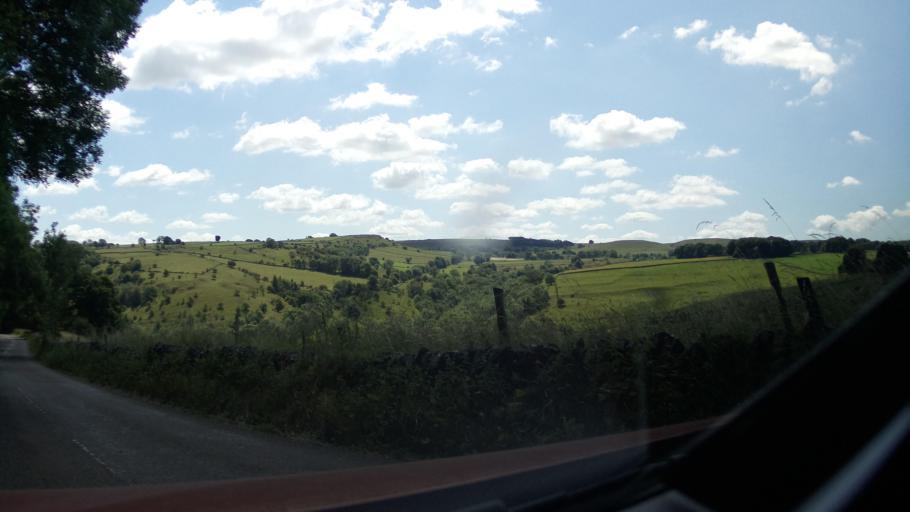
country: GB
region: England
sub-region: Derbyshire
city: Tideswell
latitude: 53.2594
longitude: -1.8028
